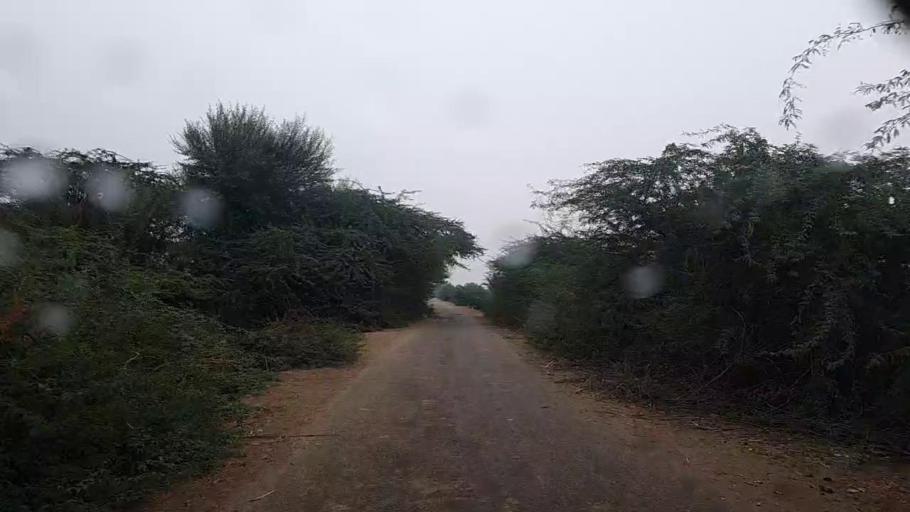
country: PK
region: Sindh
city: Ranipur
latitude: 27.2668
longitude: 68.5659
